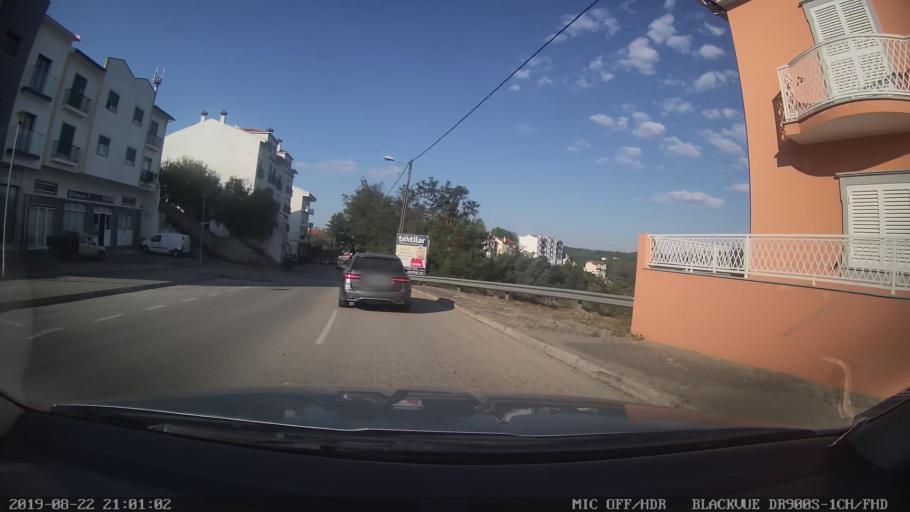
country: PT
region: Castelo Branco
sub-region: Serta
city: Serta
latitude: 39.8127
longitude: -8.0951
